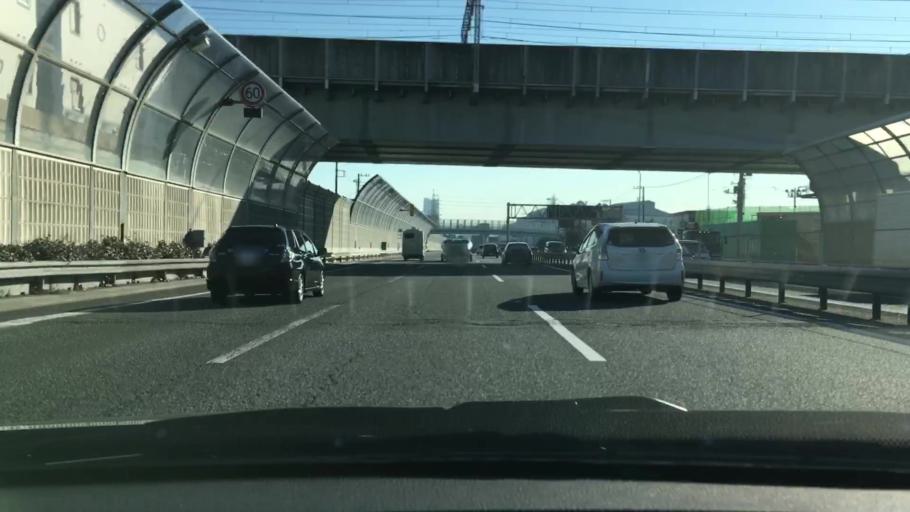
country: JP
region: Chiba
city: Funabashi
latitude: 35.7024
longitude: 139.9559
